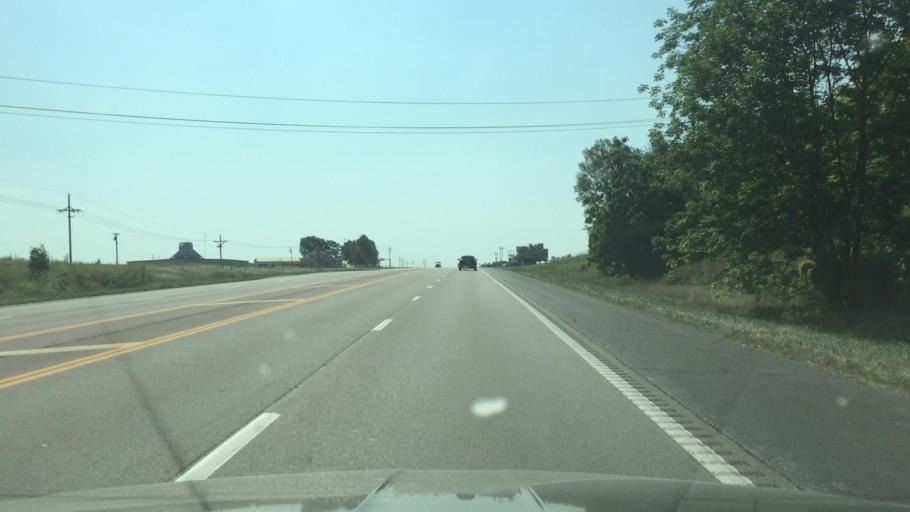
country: US
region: Missouri
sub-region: Pettis County
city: Sedalia
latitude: 38.7193
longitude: -93.2954
